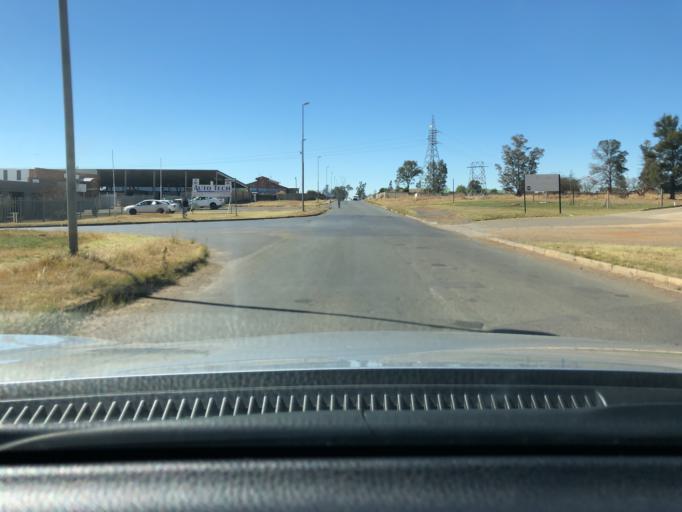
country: ZA
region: KwaZulu-Natal
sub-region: Amajuba District Municipality
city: Newcastle
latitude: -27.7605
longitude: 29.9469
